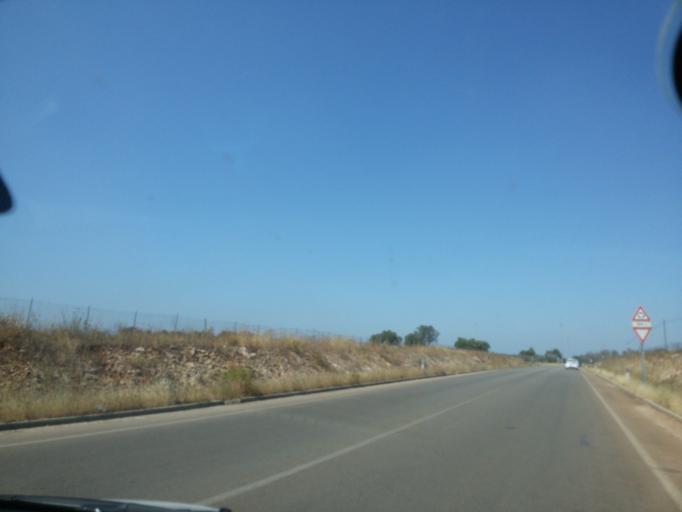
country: IT
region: Apulia
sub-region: Provincia di Lecce
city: Porto Cesareo
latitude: 40.2330
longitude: 17.9547
